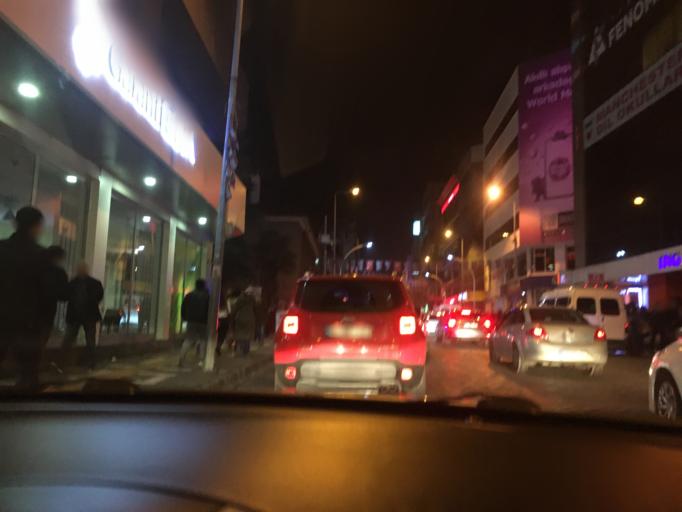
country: TR
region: Trabzon
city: Trabzon
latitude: 41.0061
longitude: 39.7269
